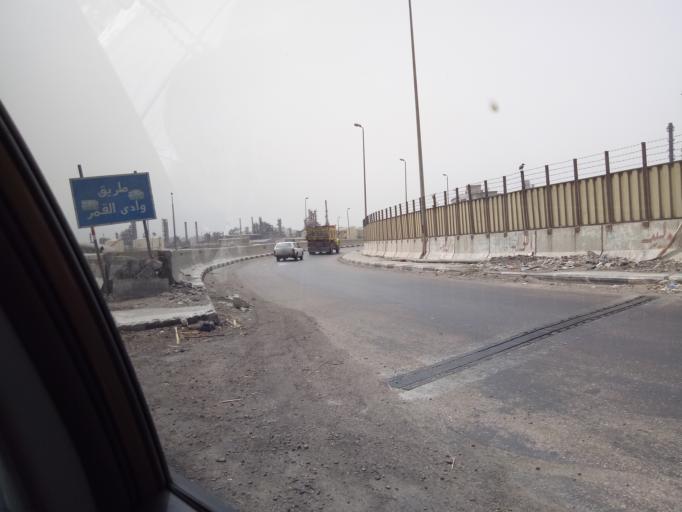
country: EG
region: Alexandria
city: Alexandria
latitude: 31.1348
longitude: 29.8513
